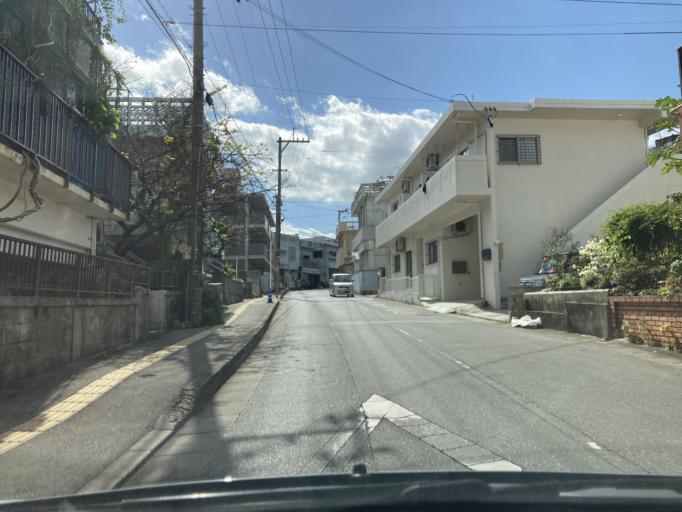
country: JP
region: Okinawa
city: Okinawa
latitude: 26.3405
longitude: 127.8016
